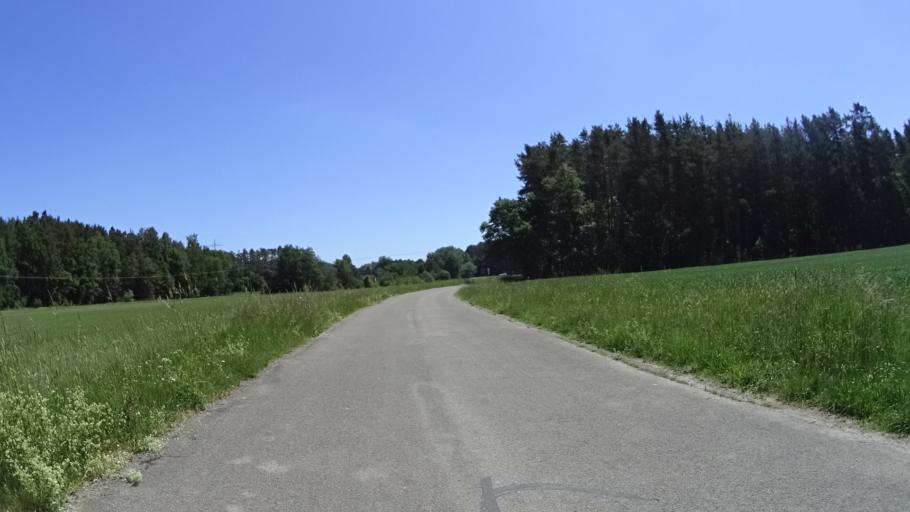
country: DE
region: Bavaria
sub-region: Regierungsbezirk Mittelfranken
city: Absberg
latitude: 49.1098
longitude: 10.9211
